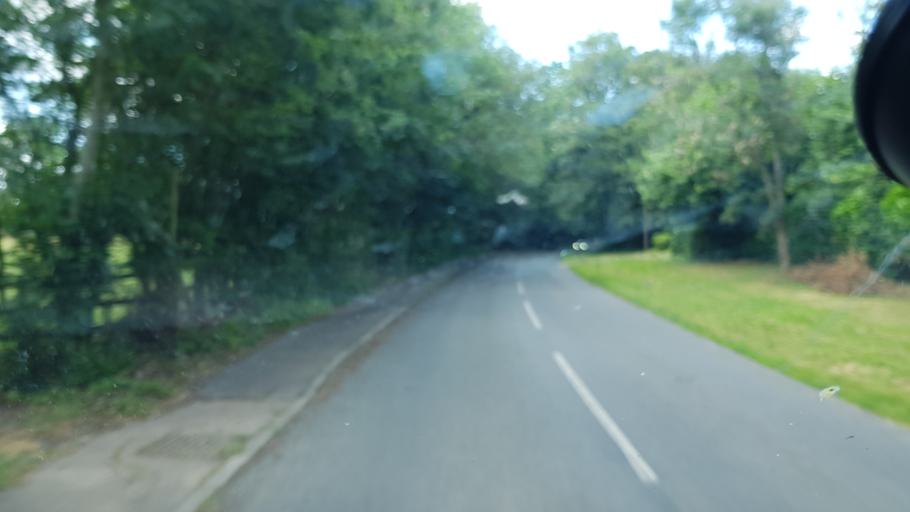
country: GB
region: England
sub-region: West Sussex
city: Rudgwick
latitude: 51.0767
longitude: -0.4534
